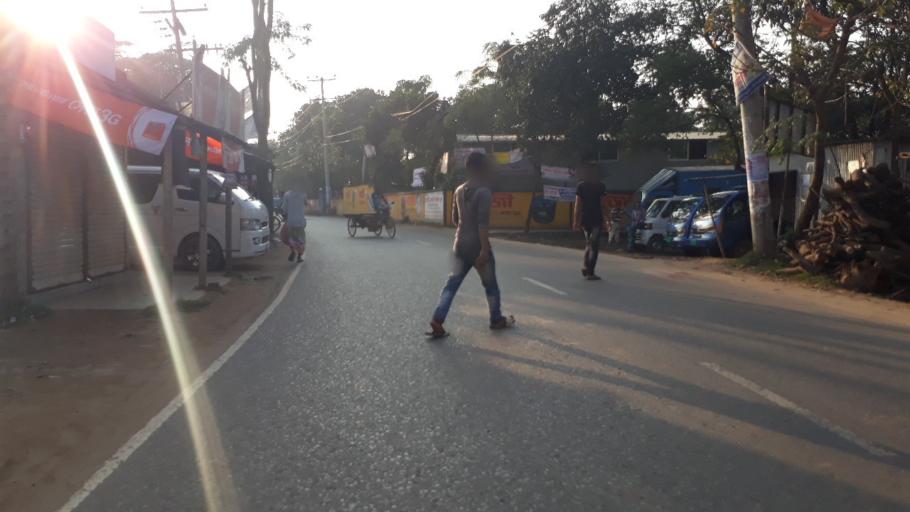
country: BD
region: Dhaka
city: Tungi
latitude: 23.8783
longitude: 90.2924
